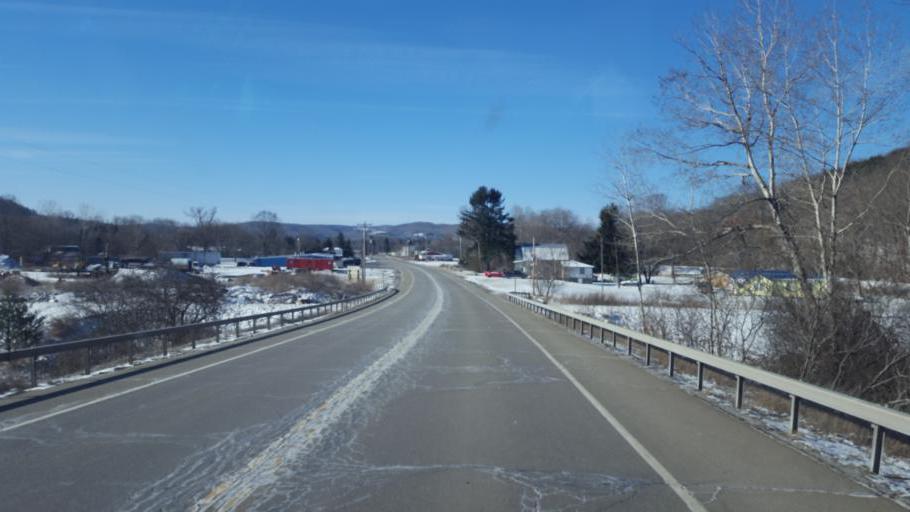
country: US
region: New York
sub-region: Allegany County
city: Wellsville
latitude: 42.1298
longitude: -77.9235
